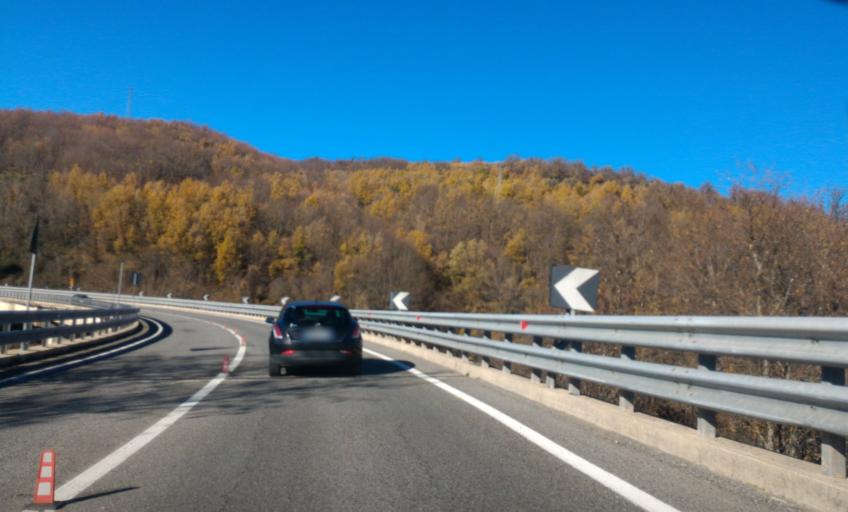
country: IT
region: Calabria
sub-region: Provincia di Cosenza
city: Celico
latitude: 39.3164
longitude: 16.3371
